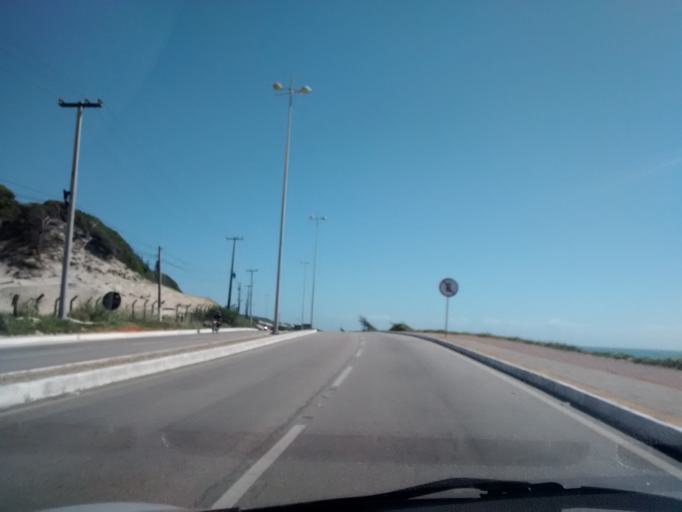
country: BR
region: Rio Grande do Norte
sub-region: Natal
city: Natal
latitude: -5.8407
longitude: -35.1821
